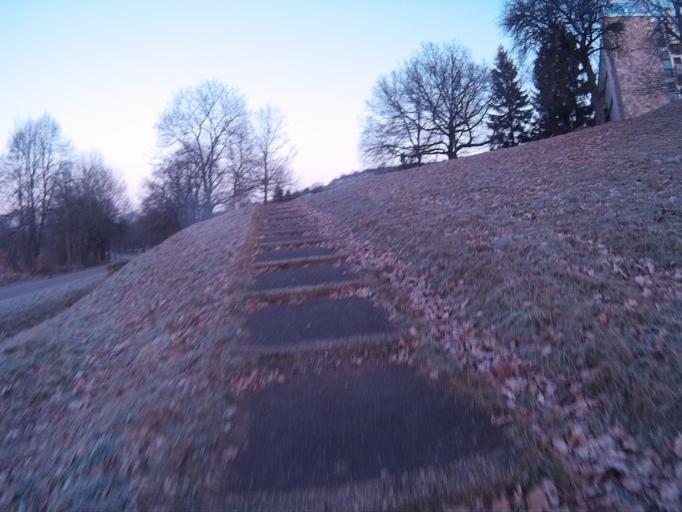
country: HU
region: Borsod-Abauj-Zemplen
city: Rudabanya
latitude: 48.4689
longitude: 20.4974
